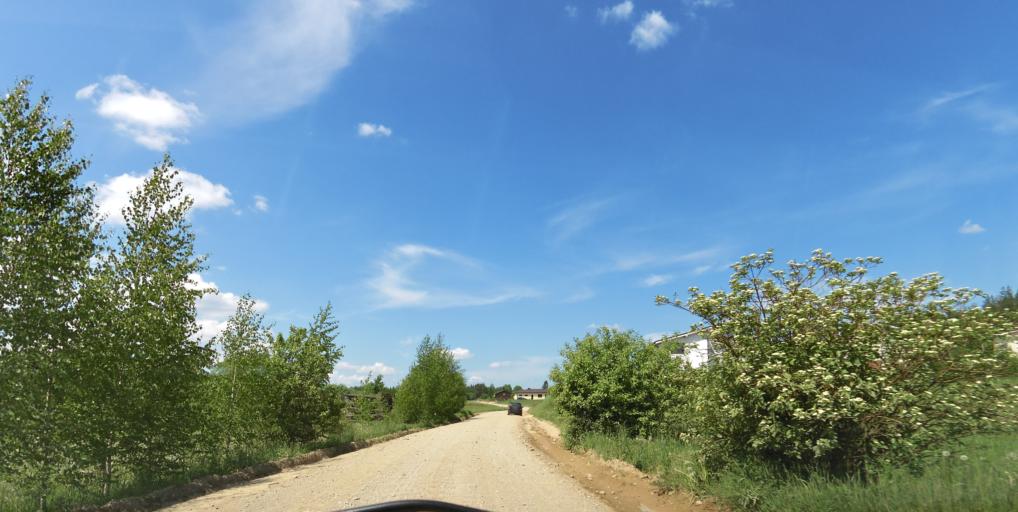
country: LT
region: Vilnius County
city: Pilaite
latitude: 54.7392
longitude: 25.1485
